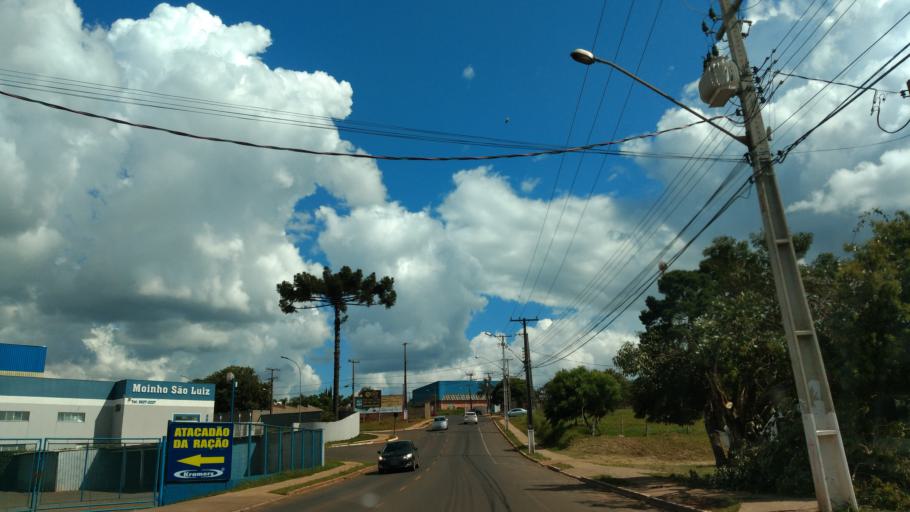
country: BR
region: Parana
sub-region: Guarapuava
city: Guarapuava
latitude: -25.3965
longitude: -51.4933
